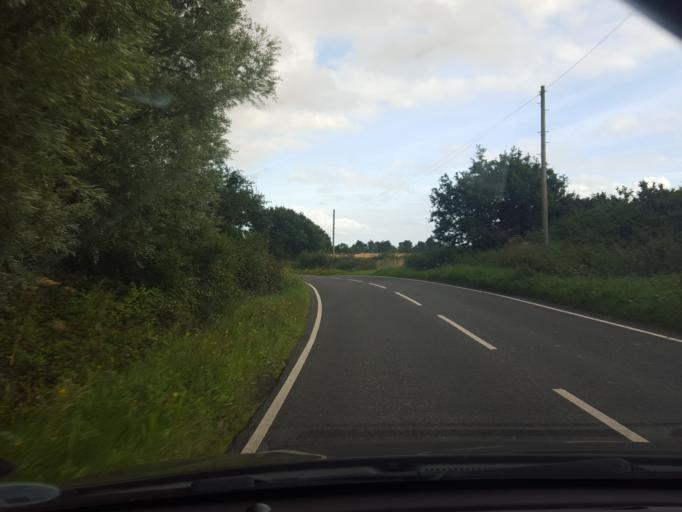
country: GB
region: England
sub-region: Essex
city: Little Clacton
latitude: 51.8311
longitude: 1.1562
